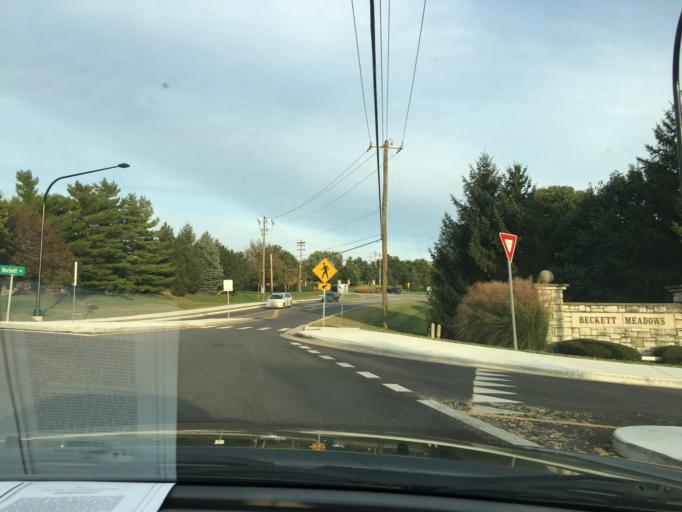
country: US
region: Ohio
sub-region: Butler County
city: Beckett Ridge
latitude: 39.3509
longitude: -84.4528
